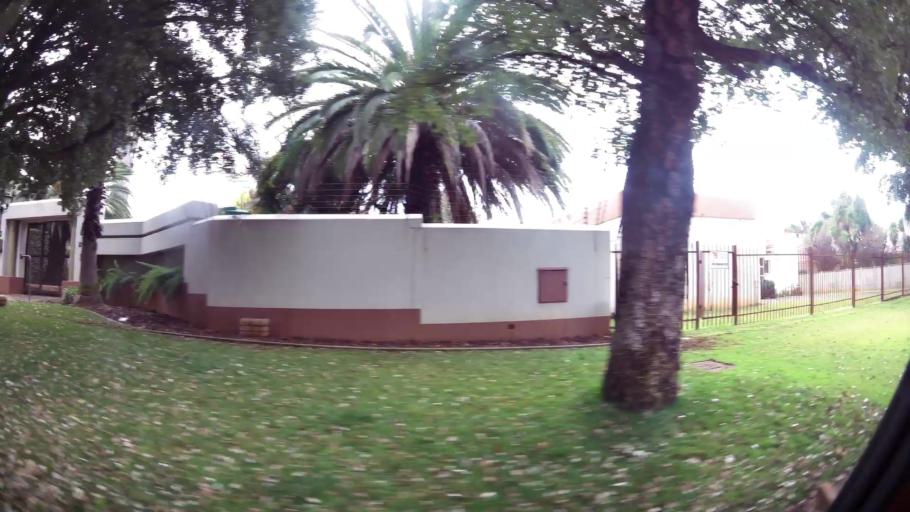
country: ZA
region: Gauteng
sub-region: Sedibeng District Municipality
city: Vanderbijlpark
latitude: -26.7346
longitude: 27.8553
